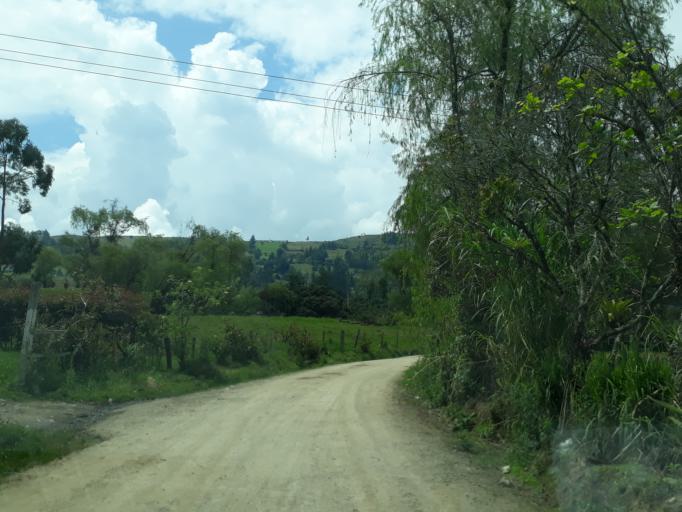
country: CO
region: Cundinamarca
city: Macheta
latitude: 5.0954
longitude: -73.5683
